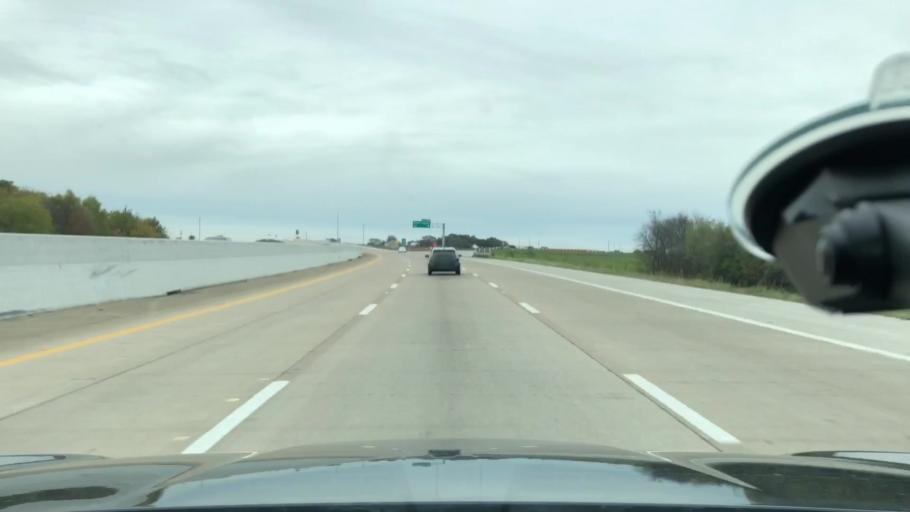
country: US
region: Texas
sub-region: Ellis County
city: Italy
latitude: 32.1723
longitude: -96.9122
